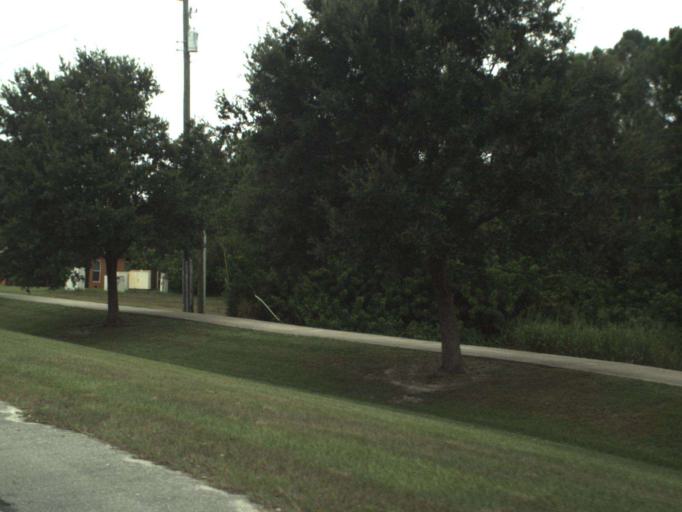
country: US
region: Florida
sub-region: Saint Lucie County
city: White City
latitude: 27.3627
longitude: -80.3552
